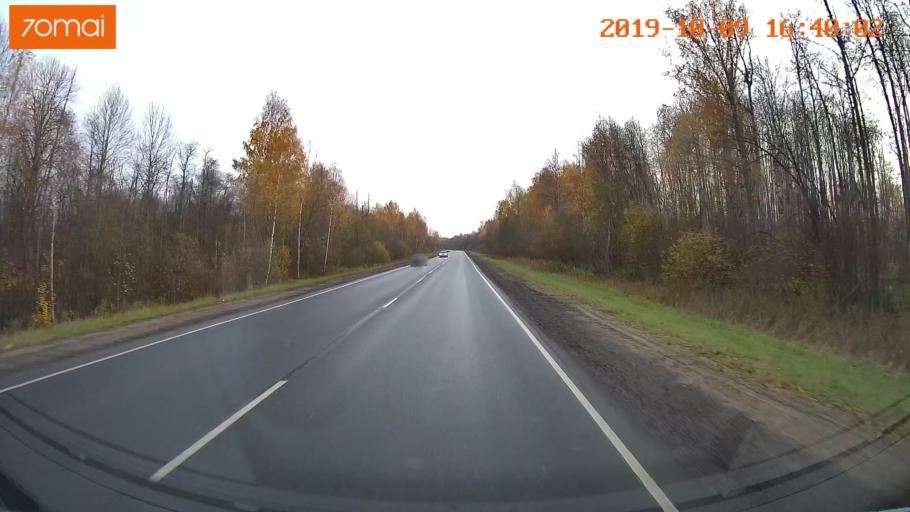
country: RU
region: Kostroma
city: Volgorechensk
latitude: 57.4893
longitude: 41.0557
